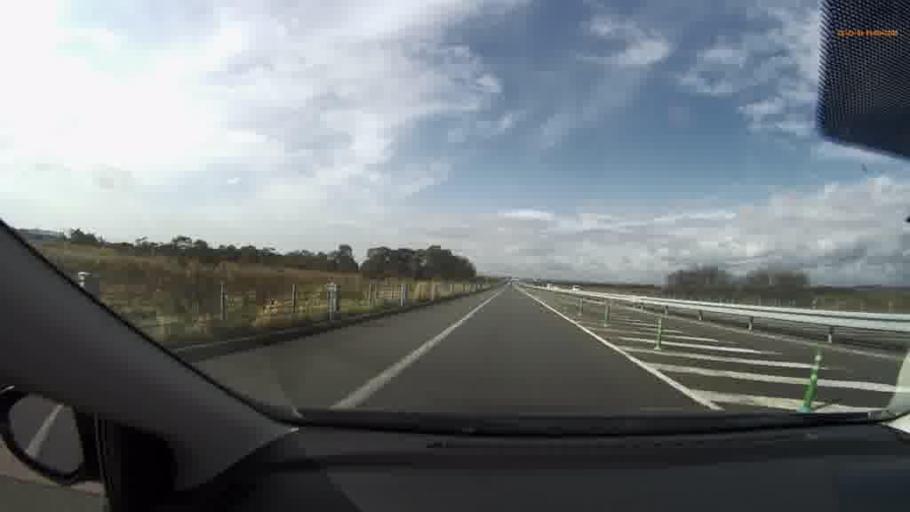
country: JP
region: Hokkaido
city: Kushiro
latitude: 43.0370
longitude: 144.3437
